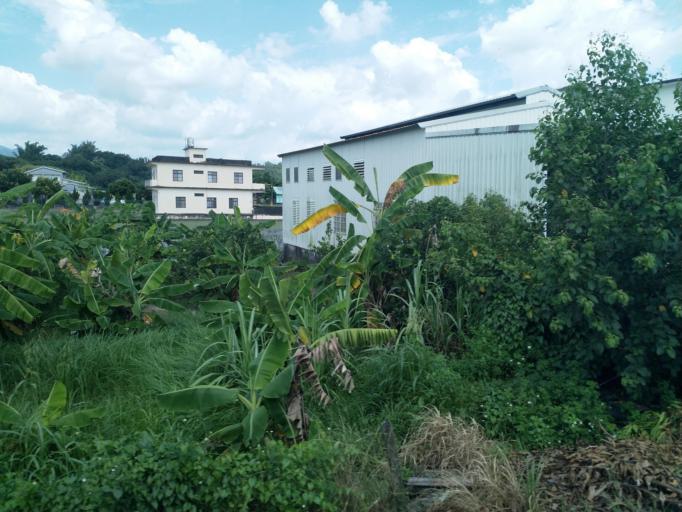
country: TW
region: Taiwan
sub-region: Pingtung
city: Pingtung
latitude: 22.8863
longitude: 120.5530
